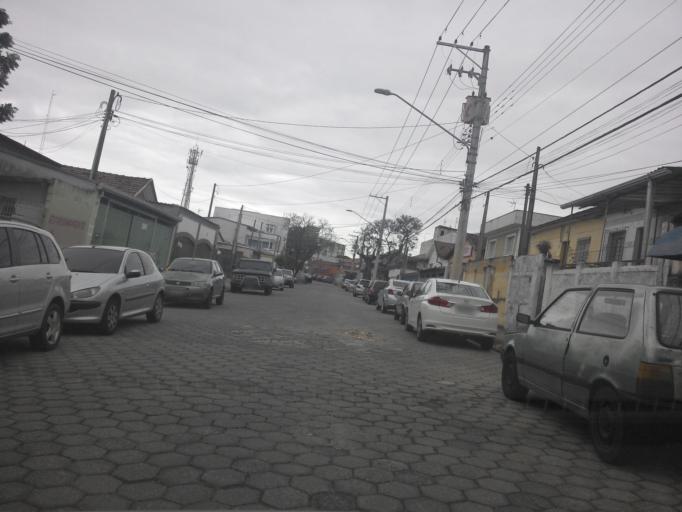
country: BR
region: Sao Paulo
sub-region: Sao Jose Dos Campos
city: Sao Jose dos Campos
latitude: -23.1833
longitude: -45.8795
